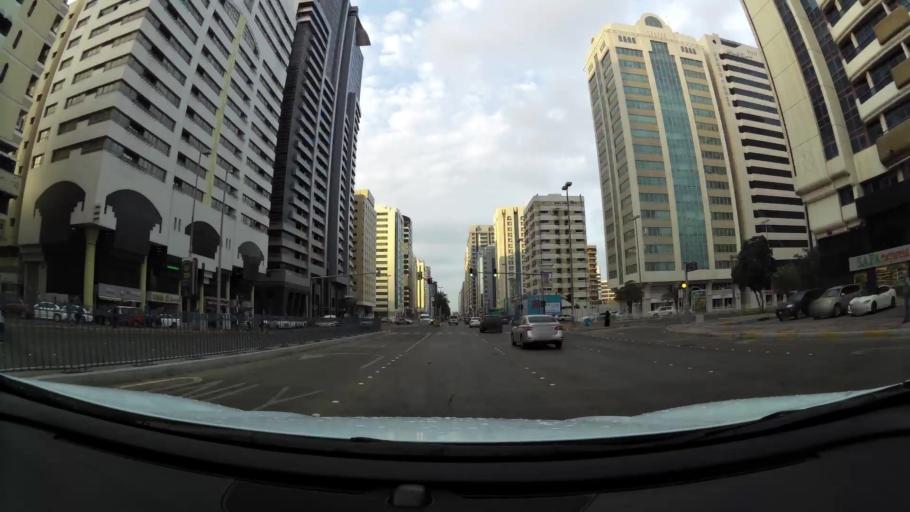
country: AE
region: Abu Dhabi
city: Abu Dhabi
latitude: 24.4779
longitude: 54.3534
